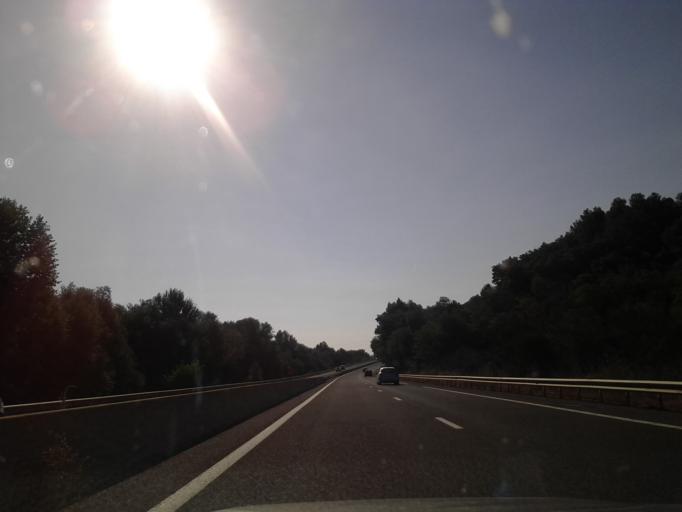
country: FR
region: Languedoc-Roussillon
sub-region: Departement des Pyrenees-Orientales
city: Pezilla-la-Riviere
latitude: 42.6836
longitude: 2.7687
